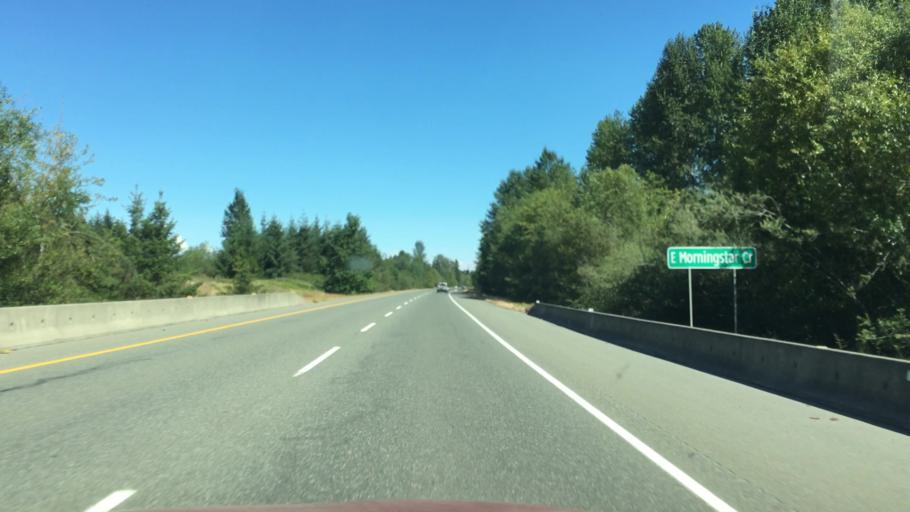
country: CA
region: British Columbia
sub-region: Regional District of Nanaimo
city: Parksville
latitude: 49.3164
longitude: -124.3743
